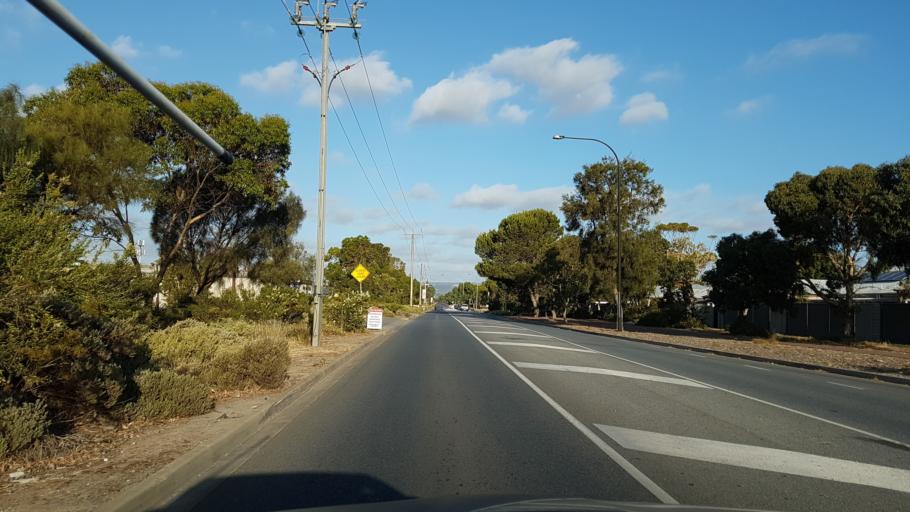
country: AU
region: South Australia
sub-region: Onkaparinga
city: Port Willunga
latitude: -35.2787
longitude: 138.4662
